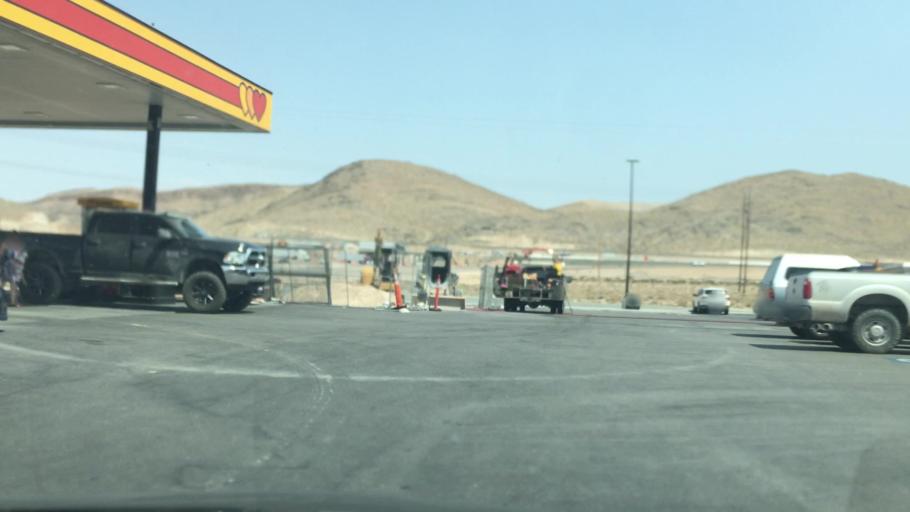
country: US
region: Nevada
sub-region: Clark County
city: Nellis Air Force Base
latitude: 36.3817
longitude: -114.8964
